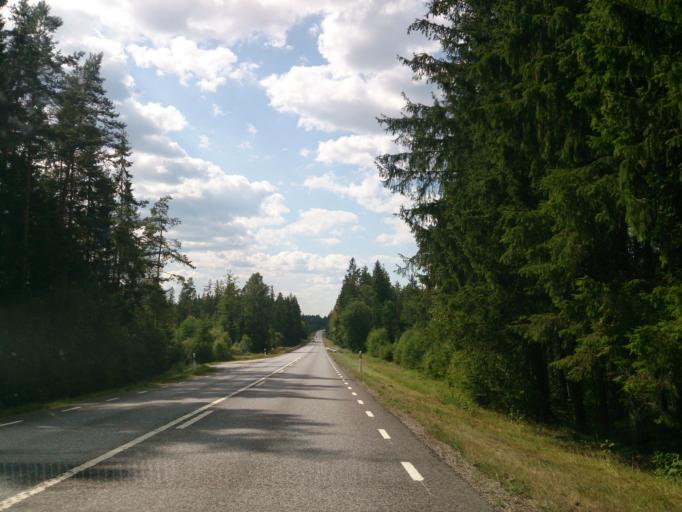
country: SE
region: Joenkoeping
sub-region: Gislaveds Kommun
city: Smalandsstenar
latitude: 57.1610
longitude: 13.4688
